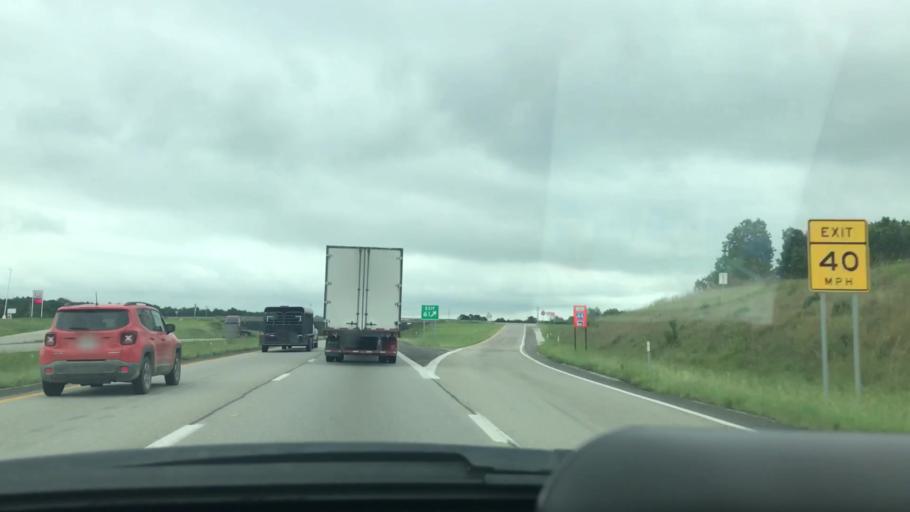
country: US
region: Missouri
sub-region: Greene County
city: Republic
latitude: 37.1859
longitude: -93.5722
